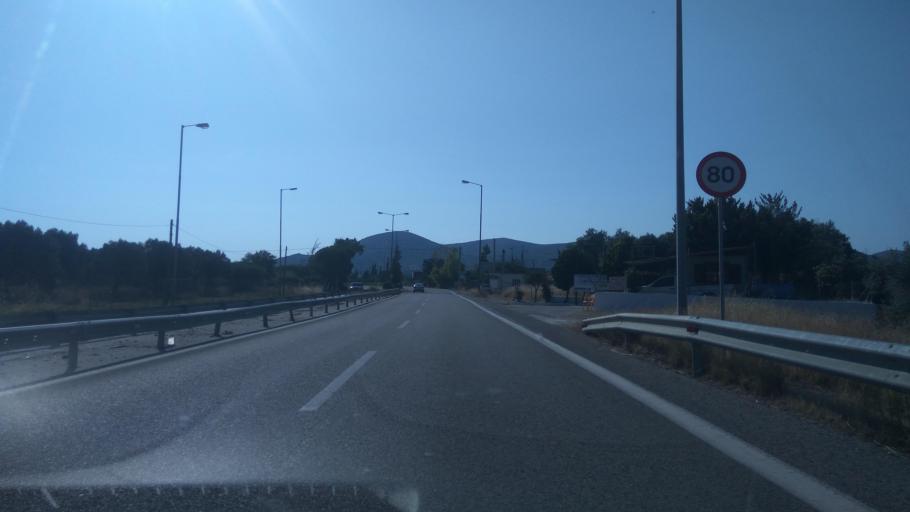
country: GR
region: Attica
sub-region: Nomarchia Anatolikis Attikis
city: Keratea
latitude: 37.8006
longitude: 23.9980
